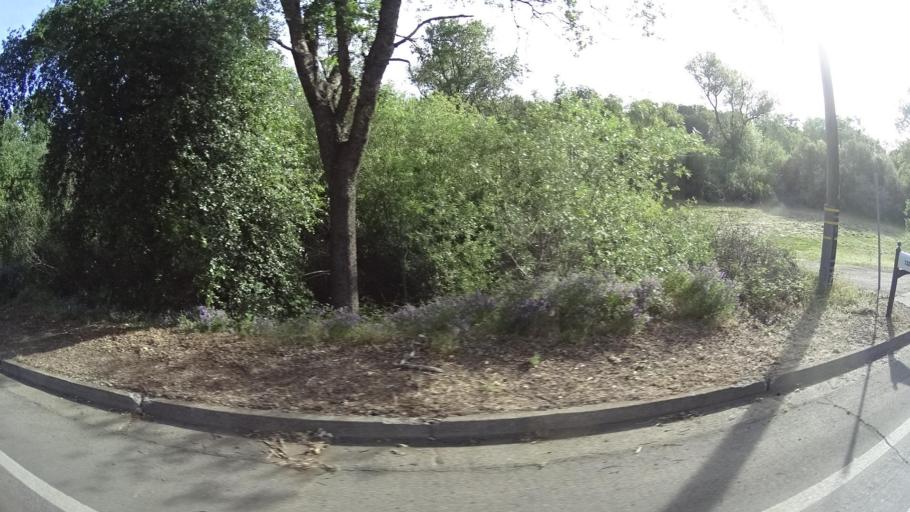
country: US
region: California
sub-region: Lake County
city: Lakeport
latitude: 39.0497
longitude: -122.9301
